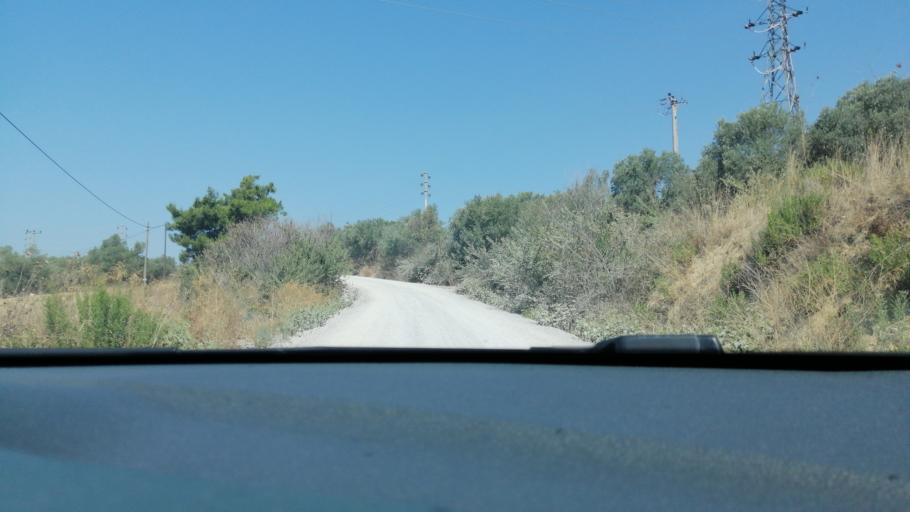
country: TR
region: Aydin
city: Davutlar
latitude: 37.7853
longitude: 27.3157
